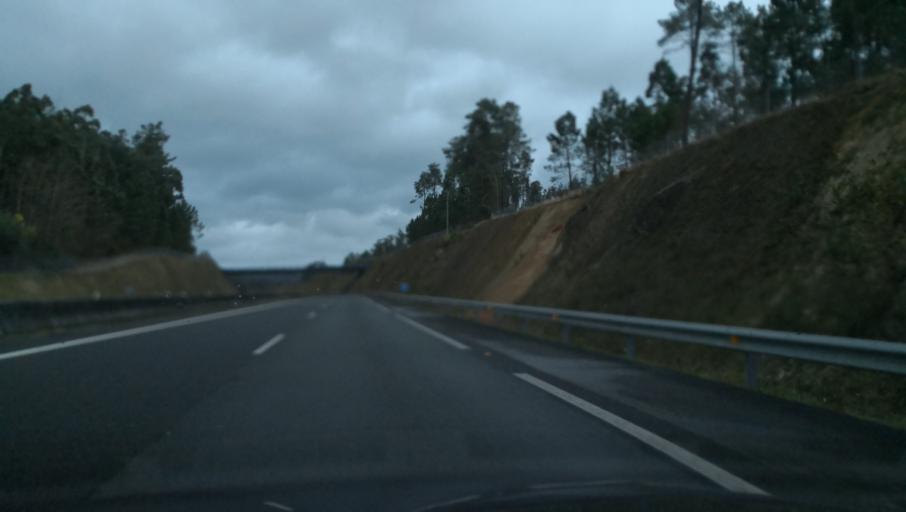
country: ES
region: Galicia
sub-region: Provincia da Coruna
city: Vedra
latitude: 42.8057
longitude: -8.4823
